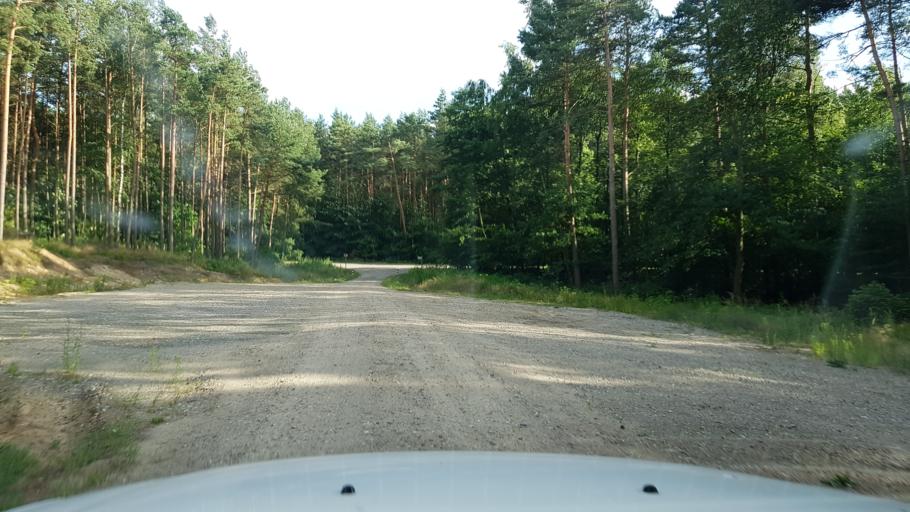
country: PL
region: West Pomeranian Voivodeship
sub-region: Powiat kolobrzeski
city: Grzybowo
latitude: 54.0927
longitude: 15.5340
